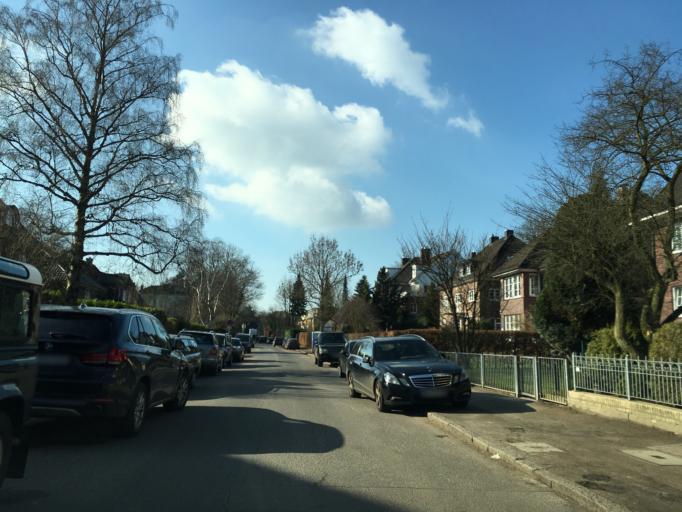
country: DE
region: Hamburg
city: Eidelstedt
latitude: 53.5619
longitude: 9.8766
